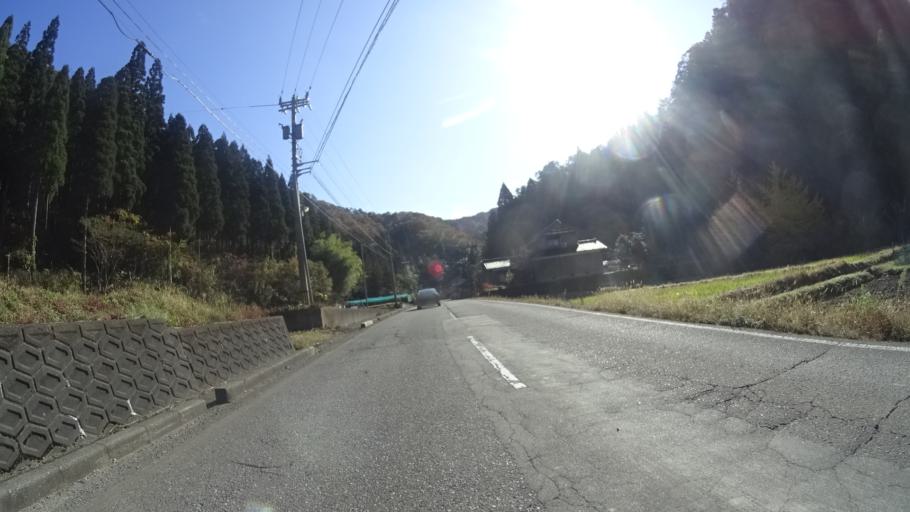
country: JP
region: Ishikawa
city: Tsurugi-asahimachi
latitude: 36.3744
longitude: 136.5686
